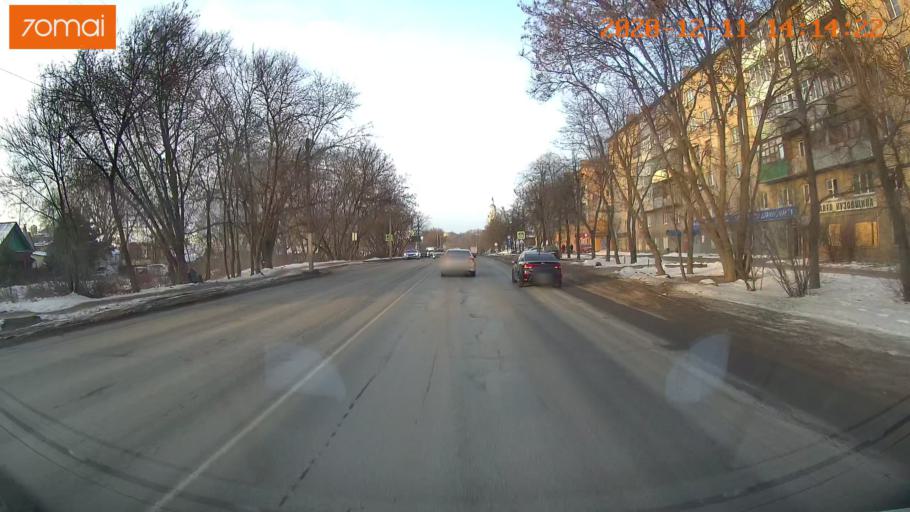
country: RU
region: Kostroma
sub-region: Kostromskoy Rayon
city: Kostroma
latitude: 57.7522
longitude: 40.9519
